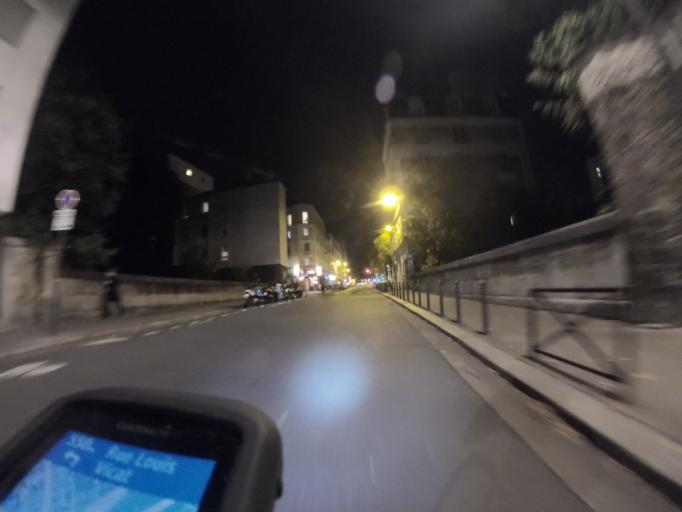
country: FR
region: Ile-de-France
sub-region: Departement des Hauts-de-Seine
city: Malakoff
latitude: 48.8301
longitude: 2.3019
